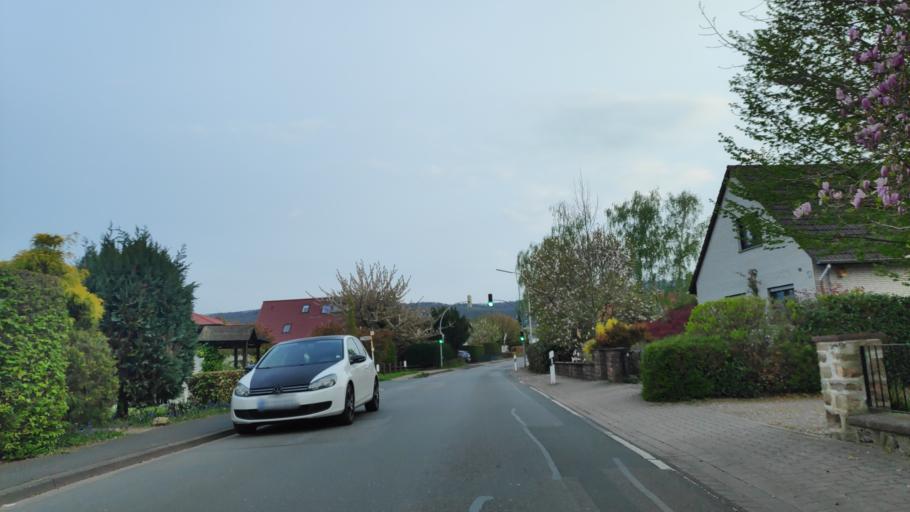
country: DE
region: North Rhine-Westphalia
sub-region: Regierungsbezirk Detmold
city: Minden
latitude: 52.2710
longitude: 8.8677
